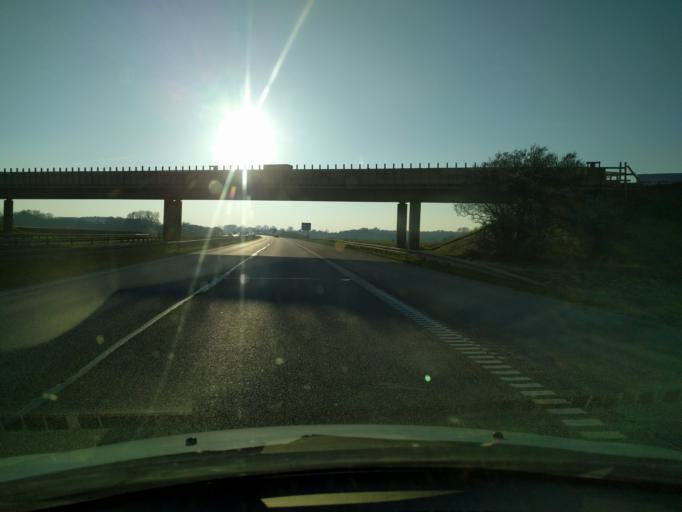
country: DK
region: Zealand
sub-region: Koge Kommune
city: Borup
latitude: 55.4580
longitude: 11.9497
